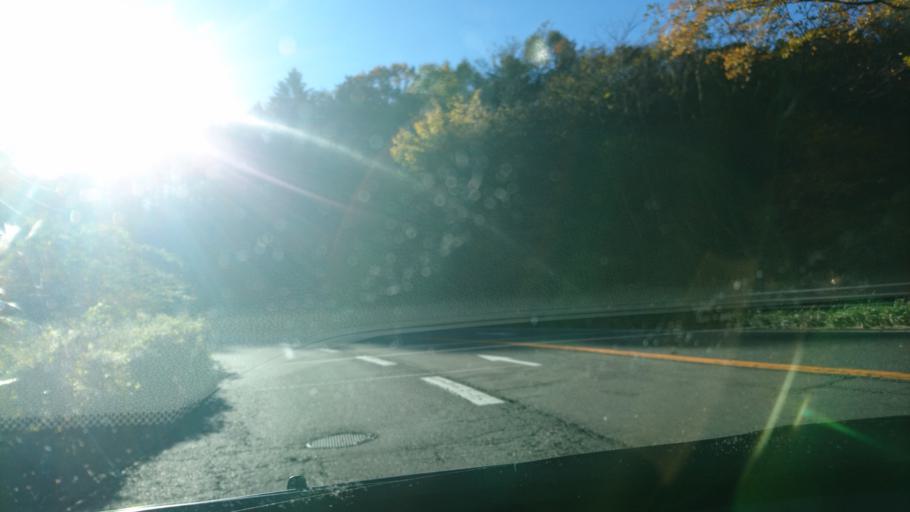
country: JP
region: Nagano
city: Saku
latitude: 36.3191
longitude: 138.6559
